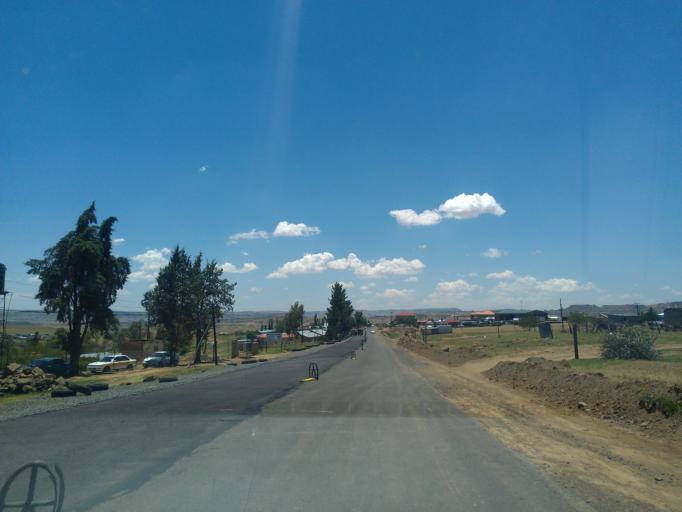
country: LS
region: Berea
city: Teyateyaneng
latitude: -29.1422
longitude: 27.7625
